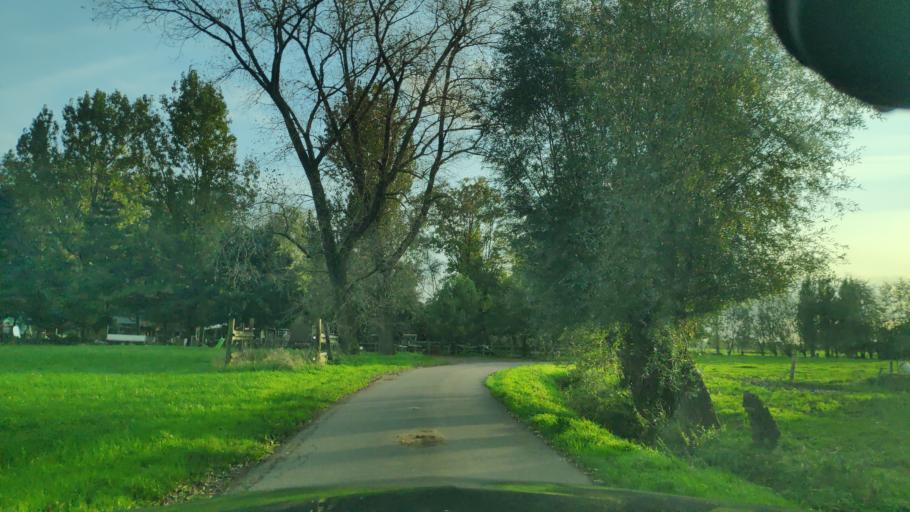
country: BE
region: Flanders
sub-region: Provincie Oost-Vlaanderen
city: Knesselare
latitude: 51.1263
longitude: 3.4425
